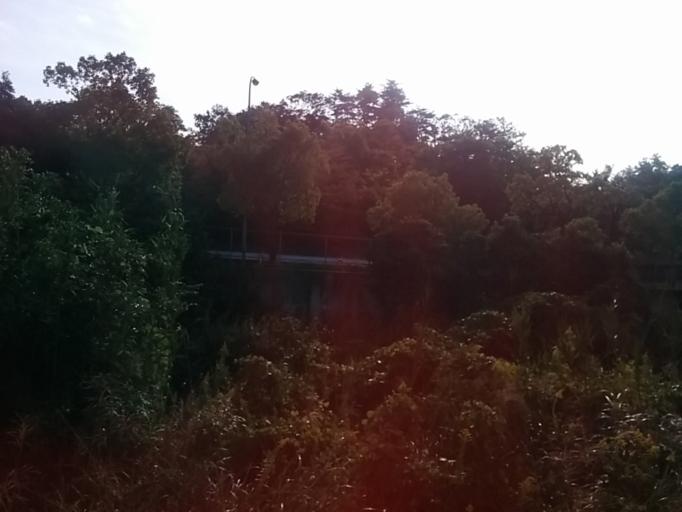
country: JP
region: Nara
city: Nara-shi
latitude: 34.7269
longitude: 135.7920
